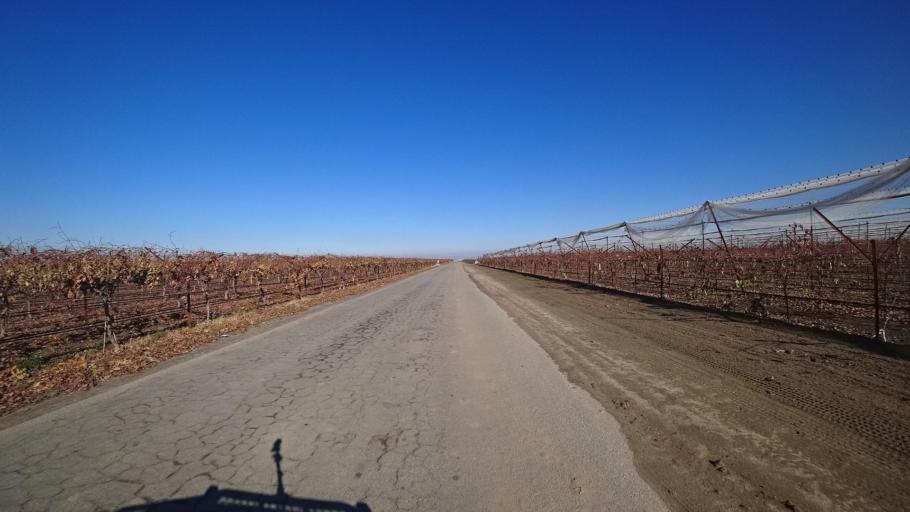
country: US
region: California
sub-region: Kern County
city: McFarland
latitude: 35.6984
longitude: -119.2675
